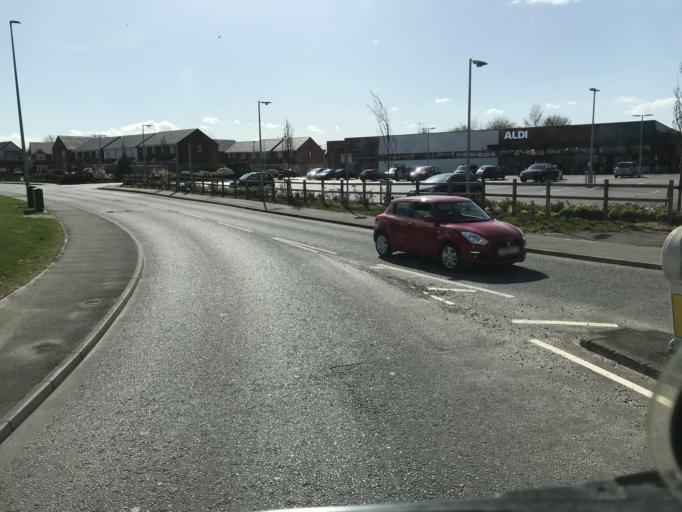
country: GB
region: Wales
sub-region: County of Flintshire
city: Hawarden
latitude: 53.1701
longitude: -2.9768
